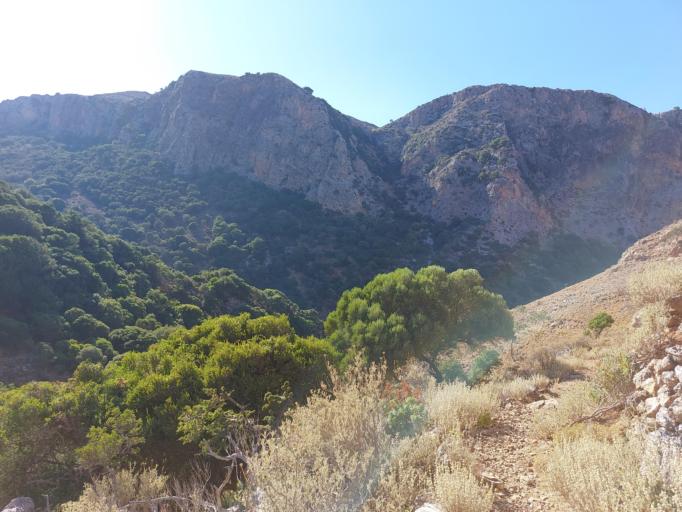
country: GR
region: Crete
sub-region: Nomos Chanias
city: Vryses
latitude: 35.4260
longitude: 23.6419
